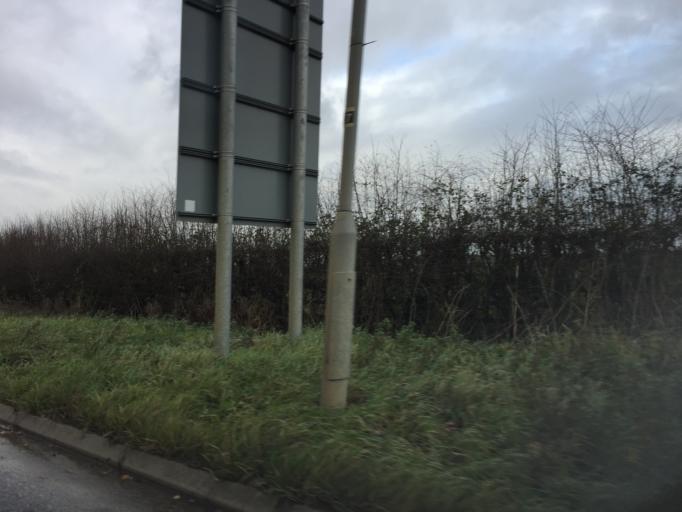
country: GB
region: England
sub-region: Wiltshire
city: Malmesbury
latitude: 51.5978
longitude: -2.1059
